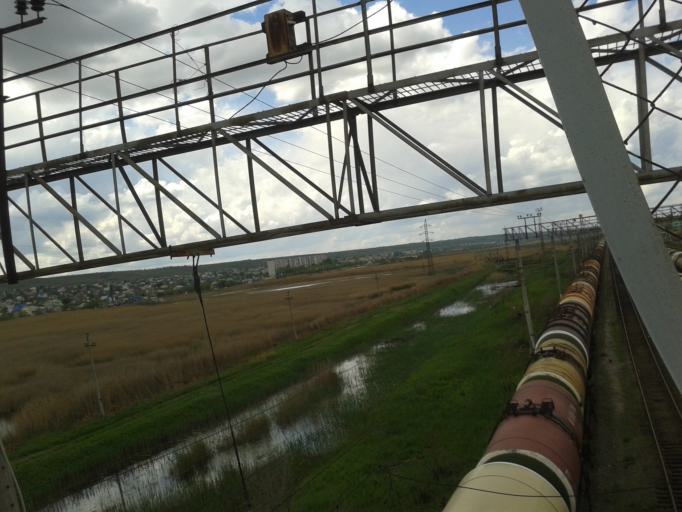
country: RU
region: Volgograd
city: Krasnoslobodsk
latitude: 48.5200
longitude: 44.5102
